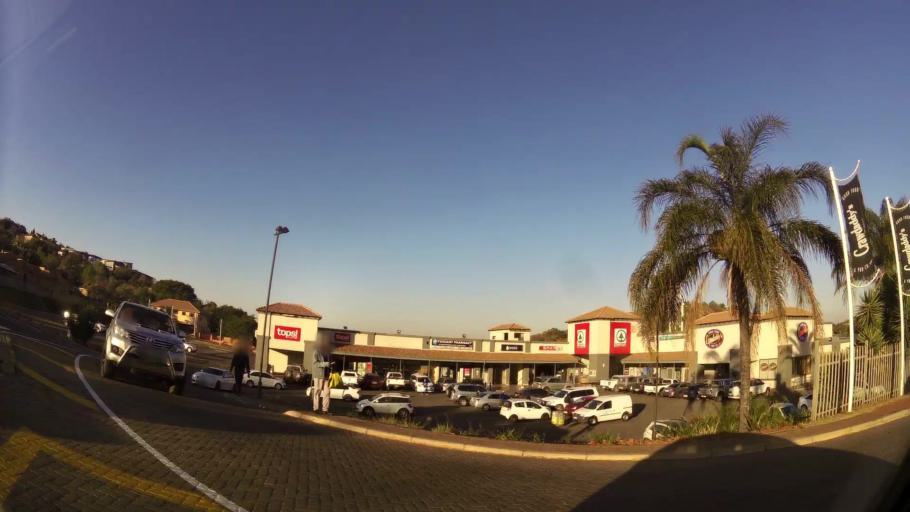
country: ZA
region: North-West
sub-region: Bojanala Platinum District Municipality
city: Rustenburg
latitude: -25.7089
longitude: 27.2399
